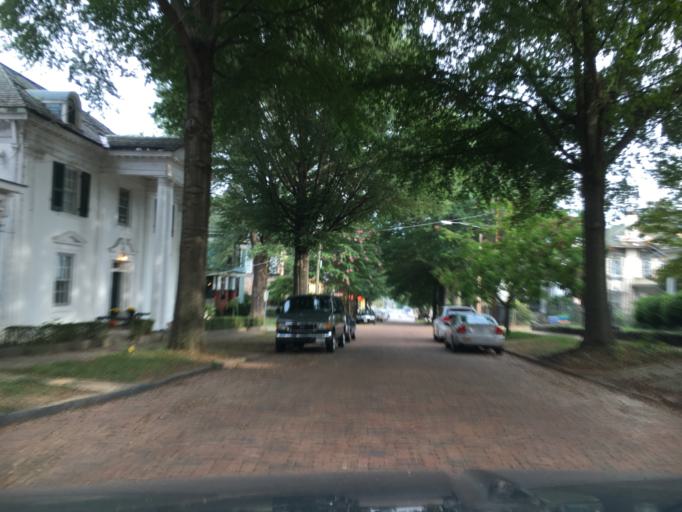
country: US
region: Virginia
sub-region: City of Lynchburg
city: Lynchburg
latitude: 37.4173
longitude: -79.1500
